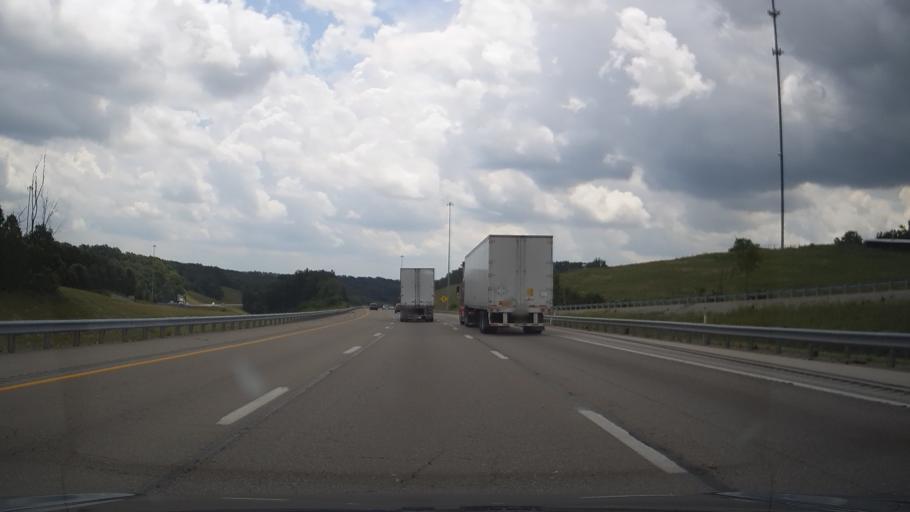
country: US
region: Kentucky
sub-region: Grant County
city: Williamstown
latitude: 38.4885
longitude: -84.5861
